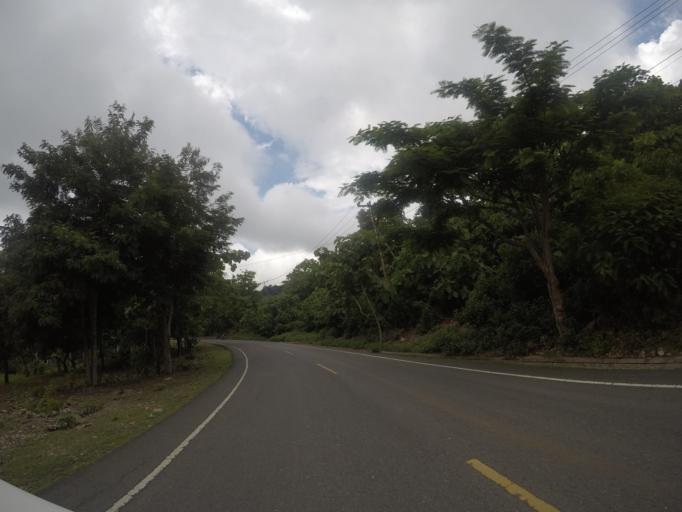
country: TL
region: Bobonaro
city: Maliana
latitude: -8.9634
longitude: 125.0362
